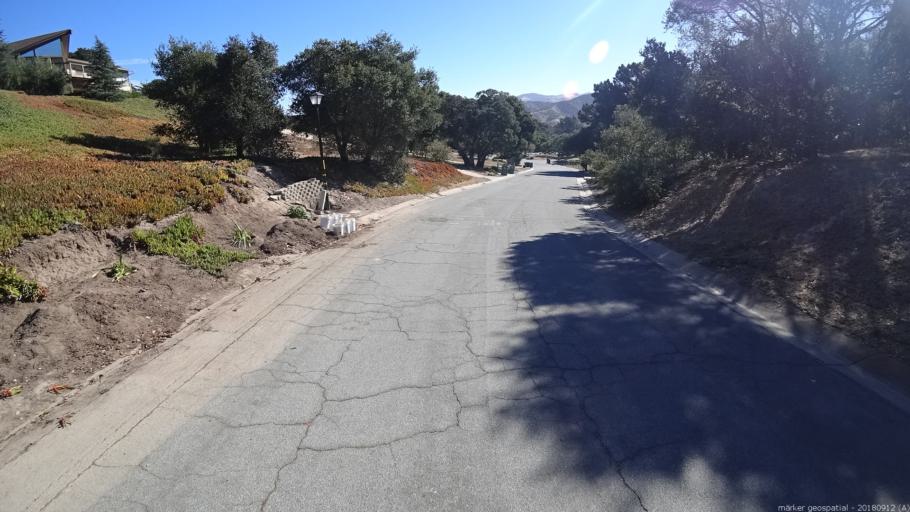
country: US
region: California
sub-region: Monterey County
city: Carmel Valley Village
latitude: 36.5634
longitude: -121.7363
